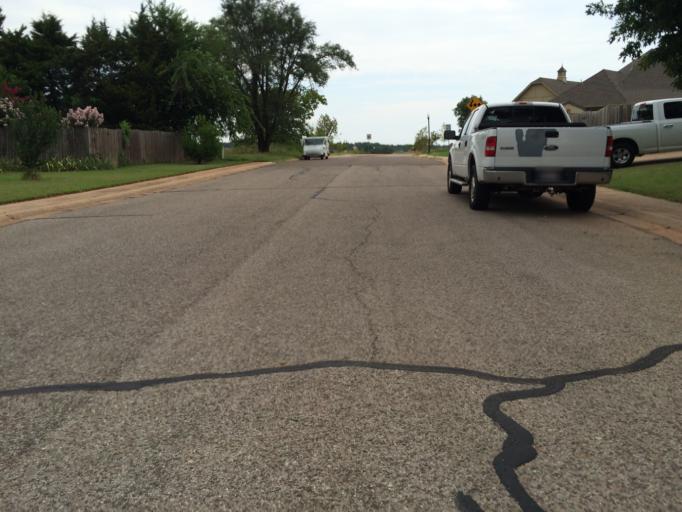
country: US
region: Oklahoma
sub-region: Cleveland County
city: Hall Park
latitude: 35.2400
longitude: -97.4132
